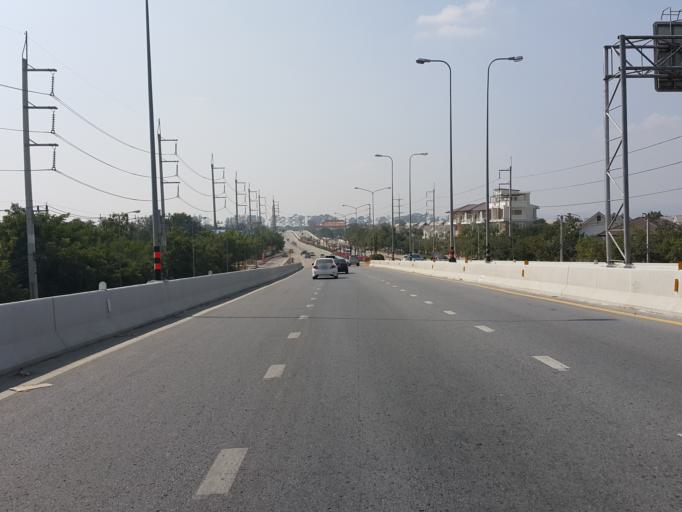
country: TH
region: Chiang Mai
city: Saraphi
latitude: 18.7524
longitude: 99.0314
